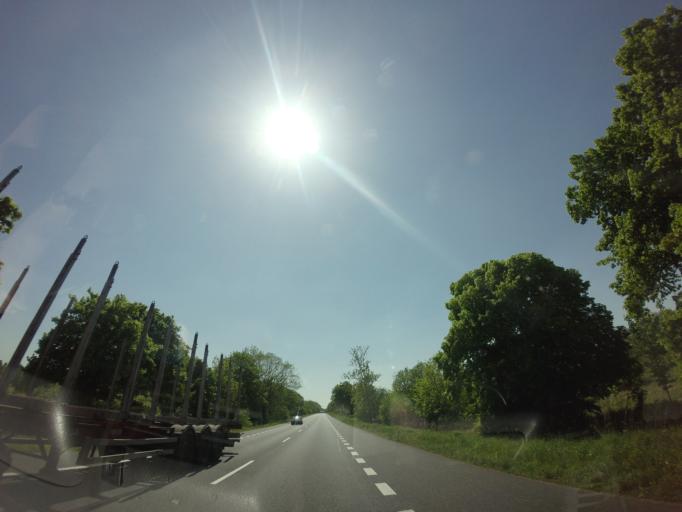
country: PL
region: West Pomeranian Voivodeship
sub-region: Powiat pyrzycki
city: Lipiany
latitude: 52.9836
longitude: 14.9781
